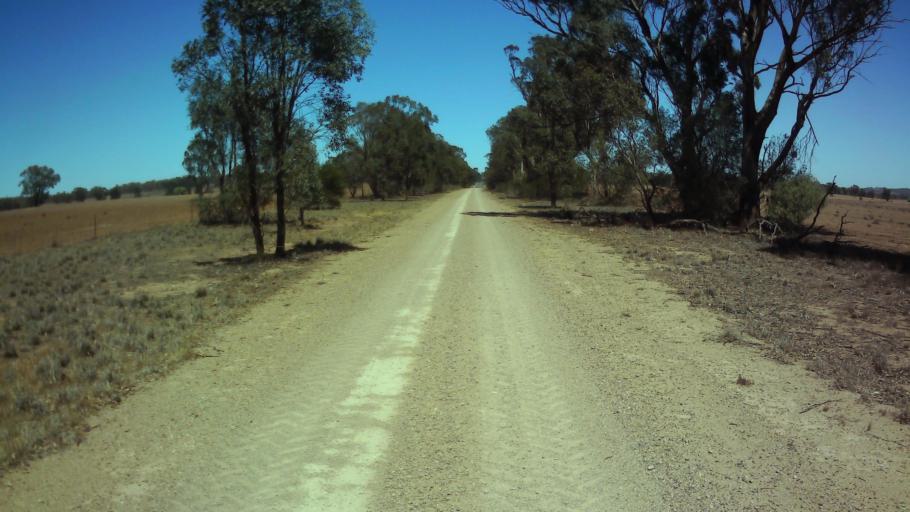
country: AU
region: New South Wales
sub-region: Forbes
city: Forbes
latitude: -33.6940
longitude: 147.8140
